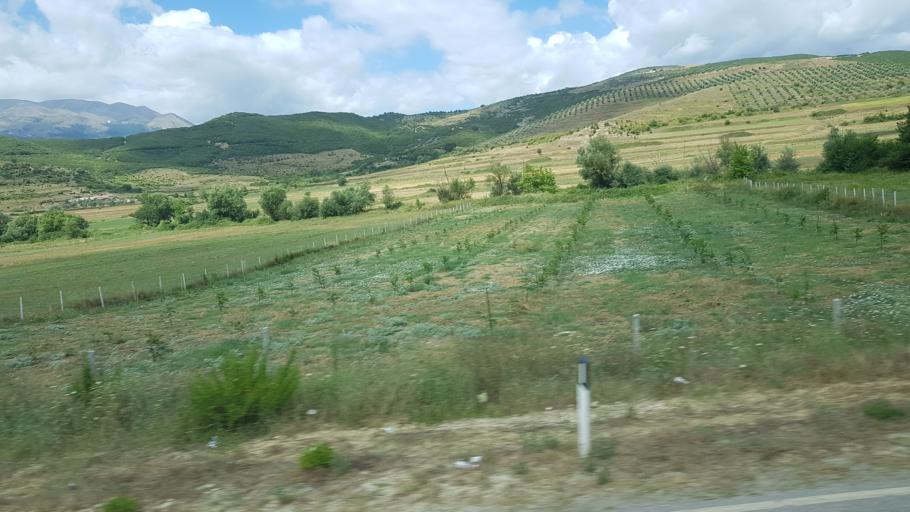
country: AL
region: Gjirokaster
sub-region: Rrethi i Tepelenes
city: Krahes
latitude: 40.4207
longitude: 19.8579
